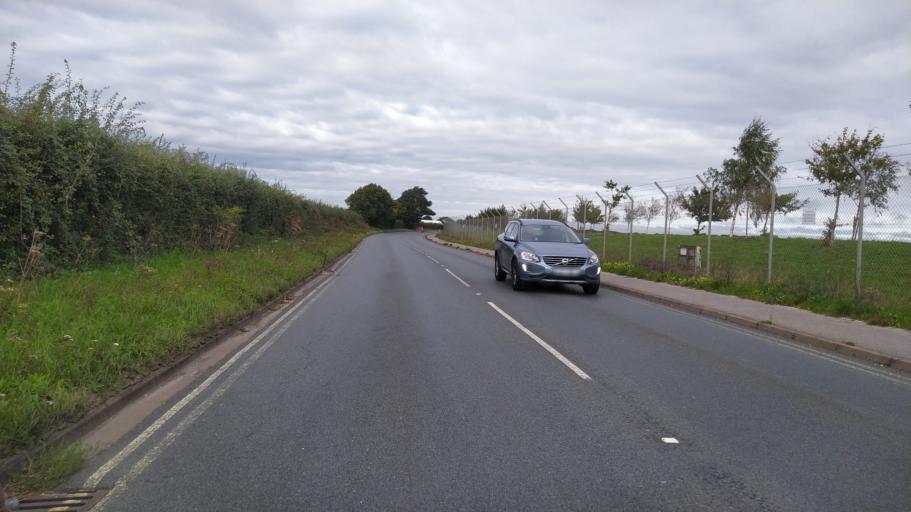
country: GB
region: England
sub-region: Dorset
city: St Leonards
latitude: 50.7753
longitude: -1.8373
